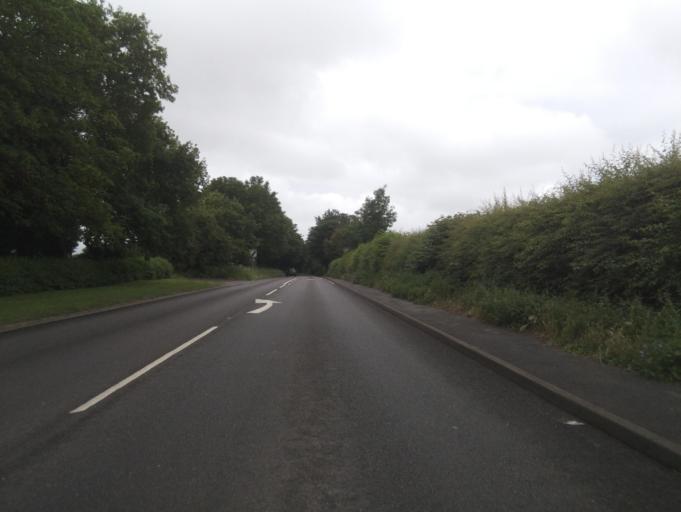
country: GB
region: England
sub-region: Staffordshire
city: Burton upon Trent
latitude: 52.8426
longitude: -1.6720
